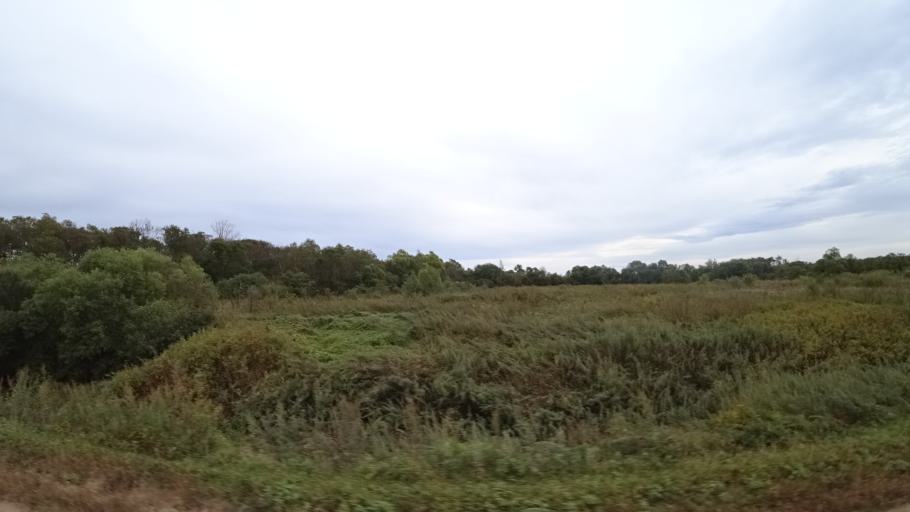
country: RU
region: Amur
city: Arkhara
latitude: 49.4343
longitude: 130.2547
